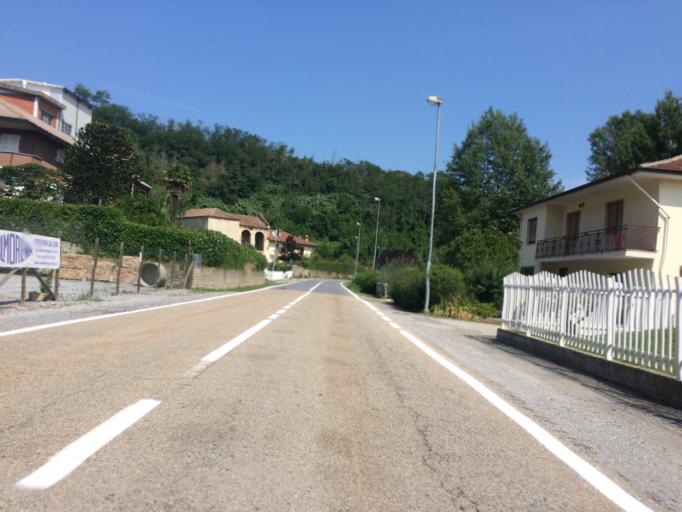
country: IT
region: Piedmont
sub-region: Provincia di Cuneo
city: Cortemilia
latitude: 44.5819
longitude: 8.1836
